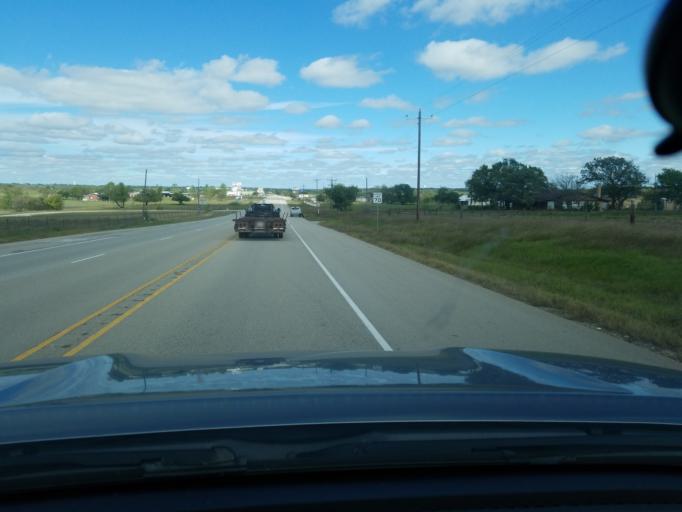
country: US
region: Texas
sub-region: Hamilton County
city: Hamilton
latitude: 31.6727
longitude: -98.1367
